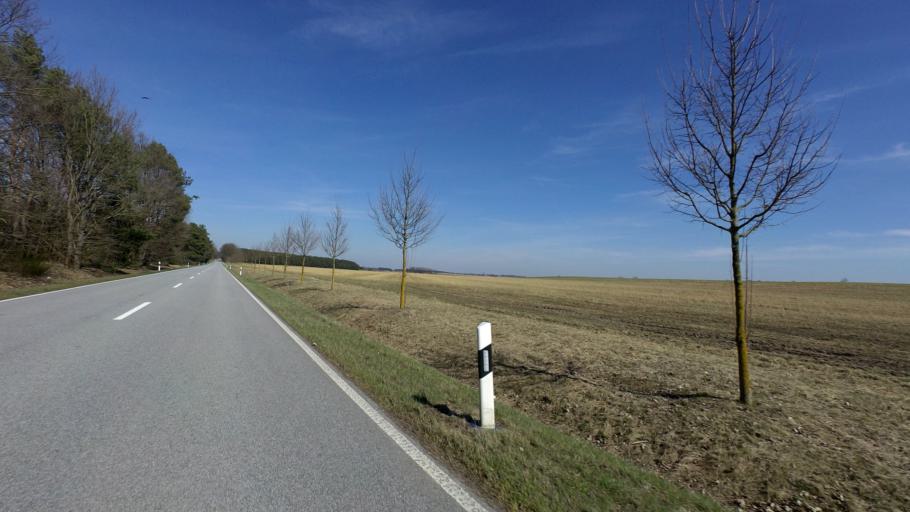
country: DE
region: Brandenburg
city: Waldsieversdorf
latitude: 52.4703
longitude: 14.0588
